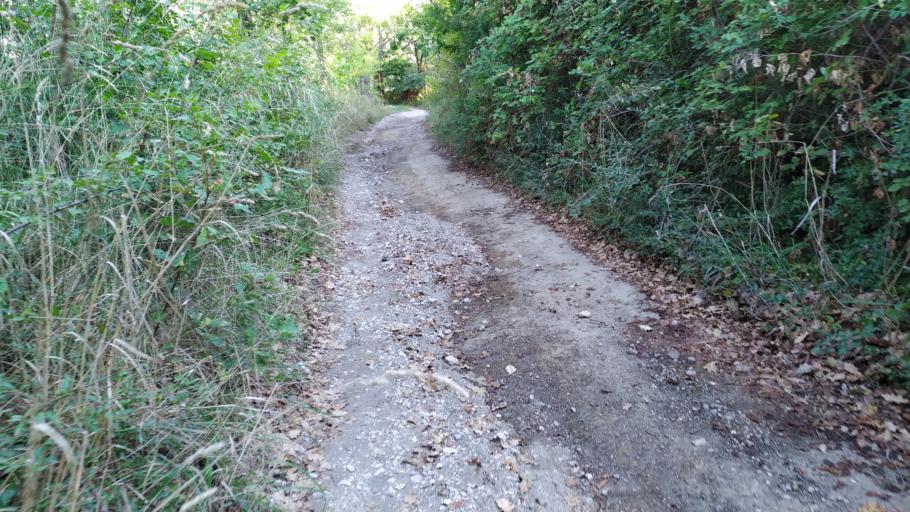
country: IT
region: Campania
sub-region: Provincia di Salerno
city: Siano
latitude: 40.8052
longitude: 14.6684
